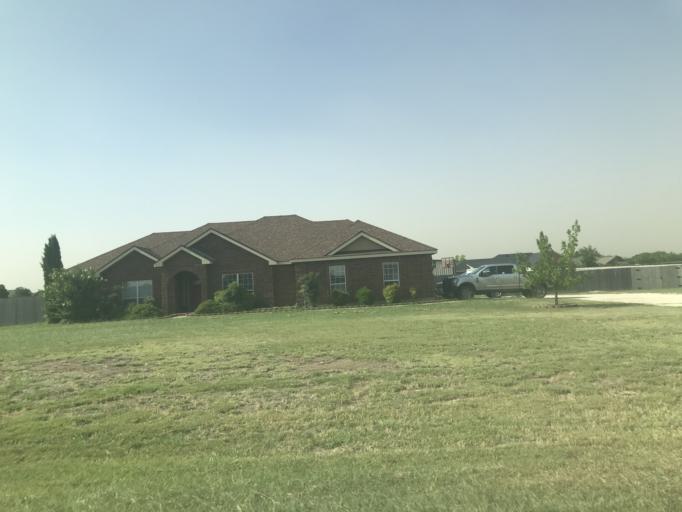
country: US
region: Texas
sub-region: Taylor County
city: Potosi
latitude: 32.3387
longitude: -99.7147
